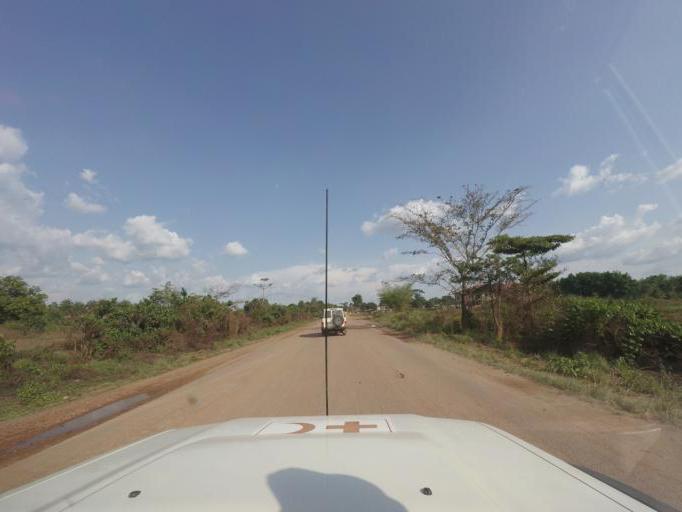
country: LR
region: Bong
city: Gbarnga
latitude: 7.0211
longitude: -9.4941
